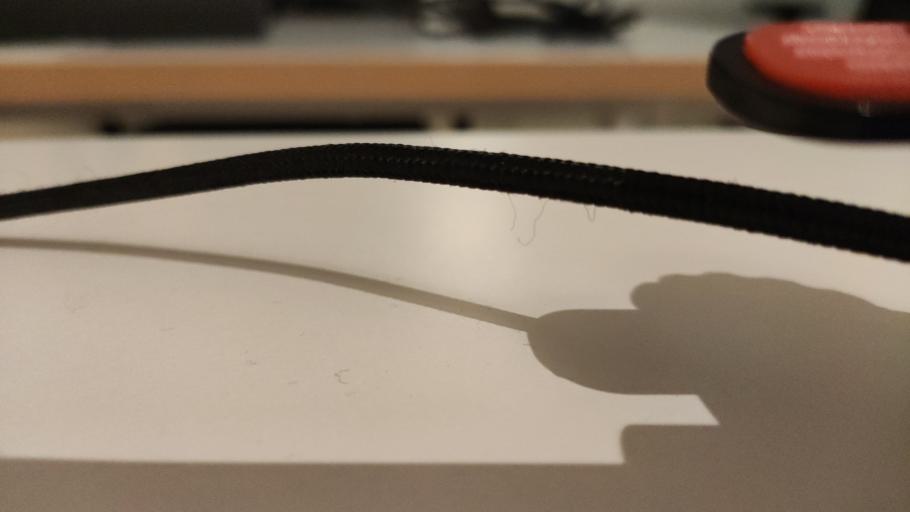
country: RU
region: Moskovskaya
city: Novoye
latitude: 55.6220
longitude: 38.9457
